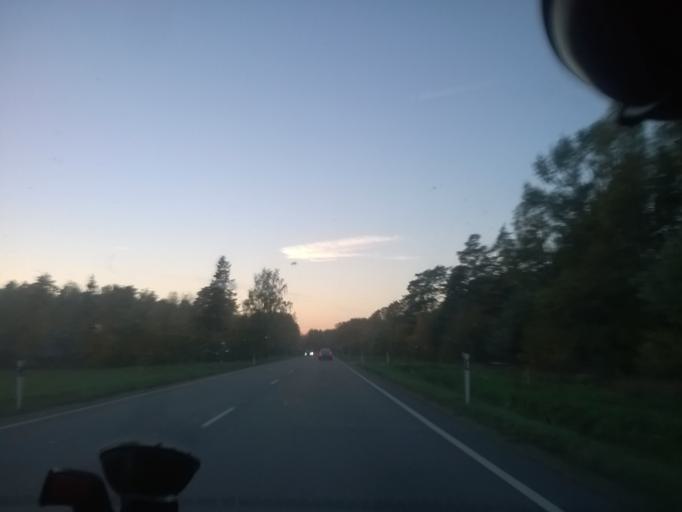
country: EE
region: Laeaene
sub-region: Ridala Parish
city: Uuemoisa
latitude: 58.9604
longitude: 23.7046
